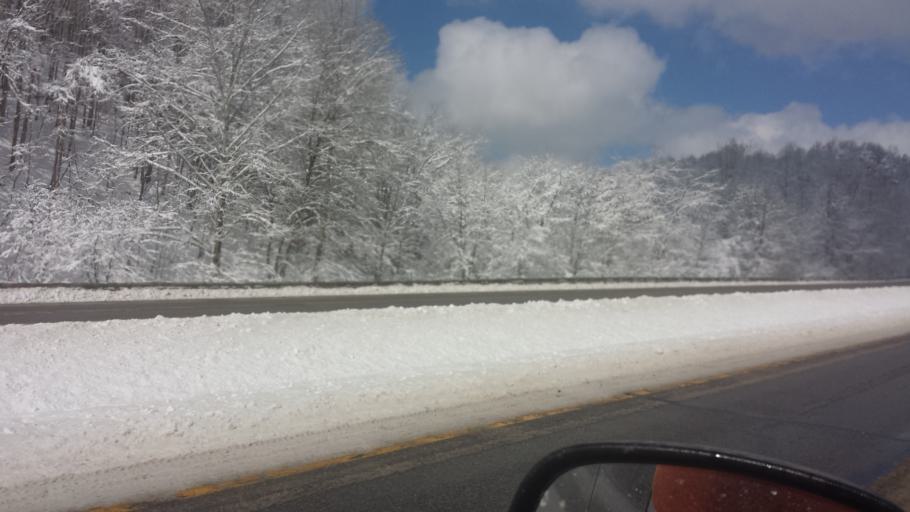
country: US
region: West Virginia
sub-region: Kanawha County
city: Sissonville
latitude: 38.5455
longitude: -81.6440
